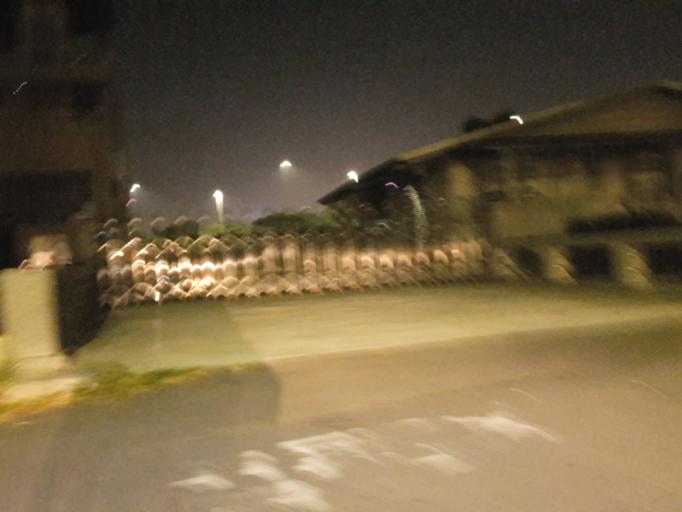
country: TW
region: Taiwan
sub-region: Hsinchu
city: Hsinchu
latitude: 24.8127
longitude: 120.9854
